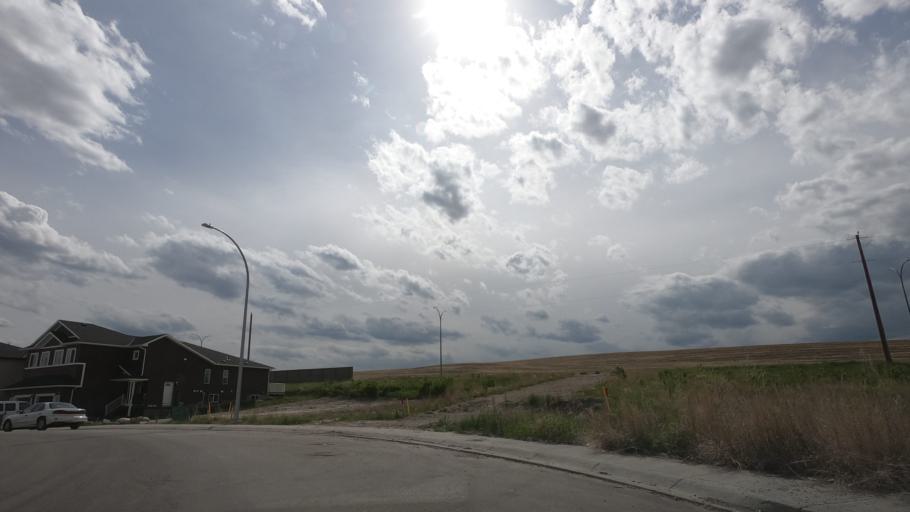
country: CA
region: Alberta
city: Airdrie
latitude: 51.2768
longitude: -114.0475
